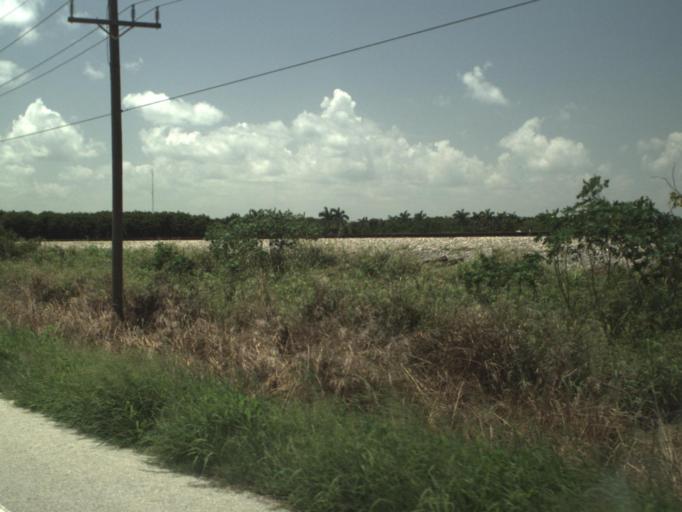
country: US
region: Florida
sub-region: Palm Beach County
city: Pahokee
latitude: 26.8215
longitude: -80.6486
